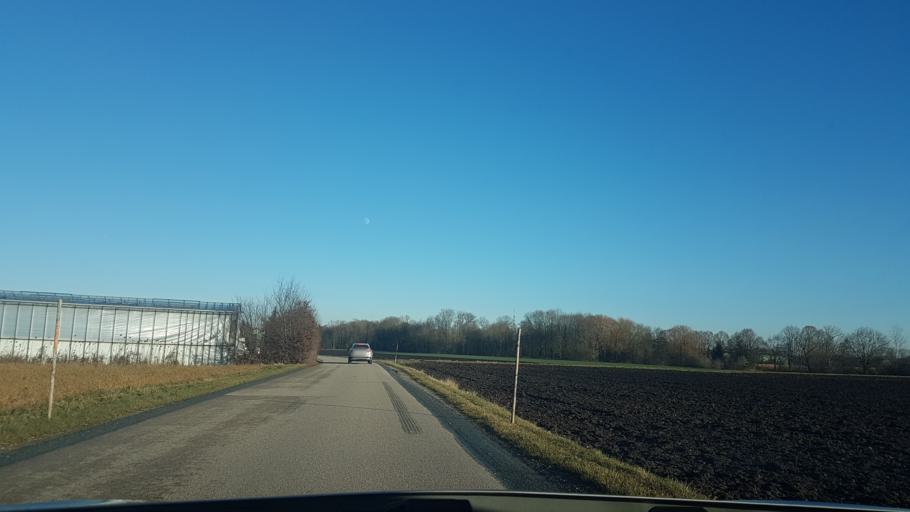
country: DE
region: Bavaria
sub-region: Upper Bavaria
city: Eichenried
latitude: 48.2805
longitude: 11.8125
